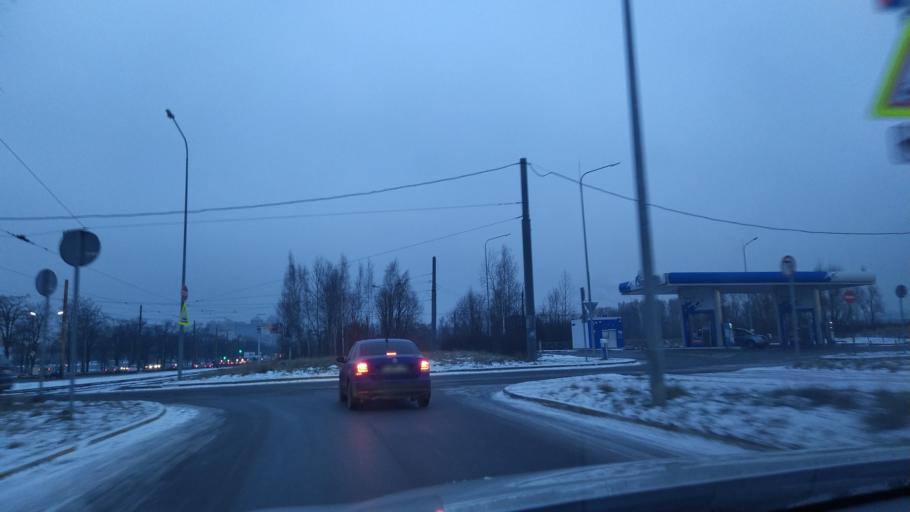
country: RU
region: St.-Petersburg
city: Grazhdanka
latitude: 60.0192
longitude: 30.4333
